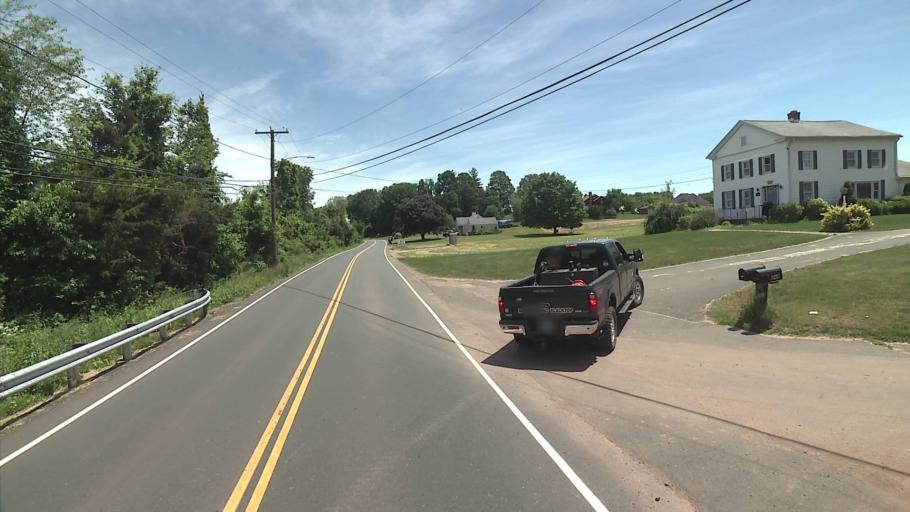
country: US
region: Connecticut
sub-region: Hartford County
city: Kensington
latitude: 41.6020
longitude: -72.8051
